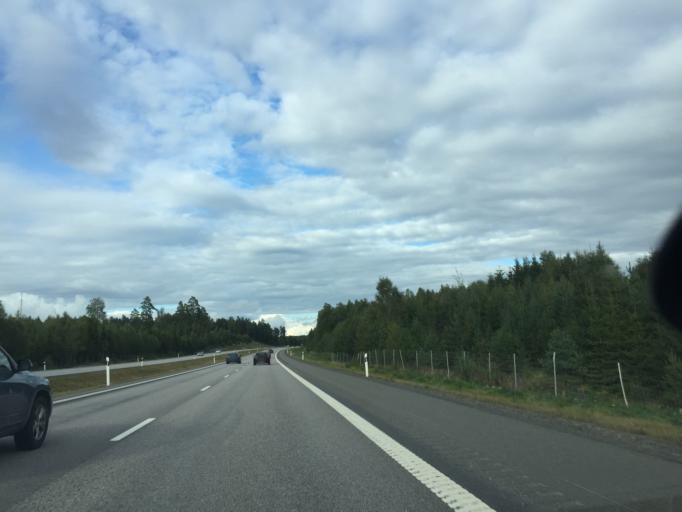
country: SE
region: OErebro
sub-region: Lindesbergs Kommun
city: Fellingsbro
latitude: 59.3628
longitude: 15.5729
